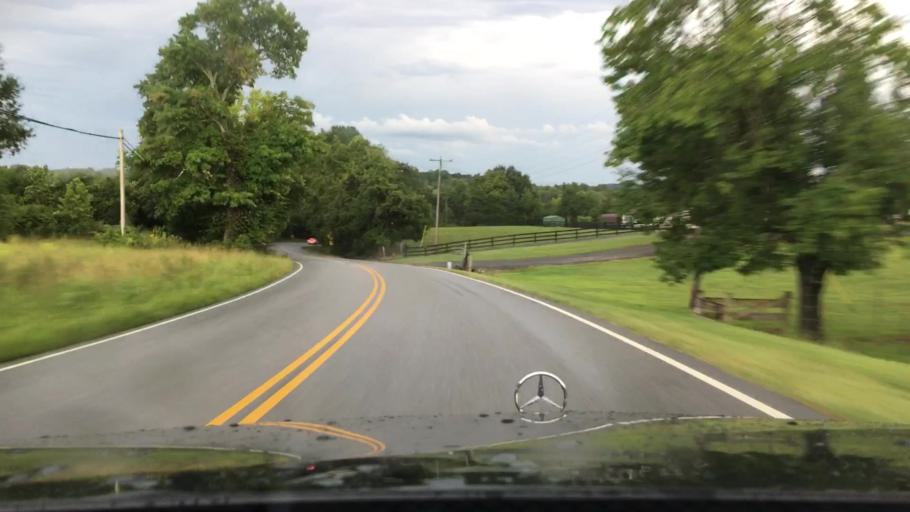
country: US
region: Virginia
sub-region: Amherst County
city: Amherst
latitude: 37.7111
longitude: -79.0233
